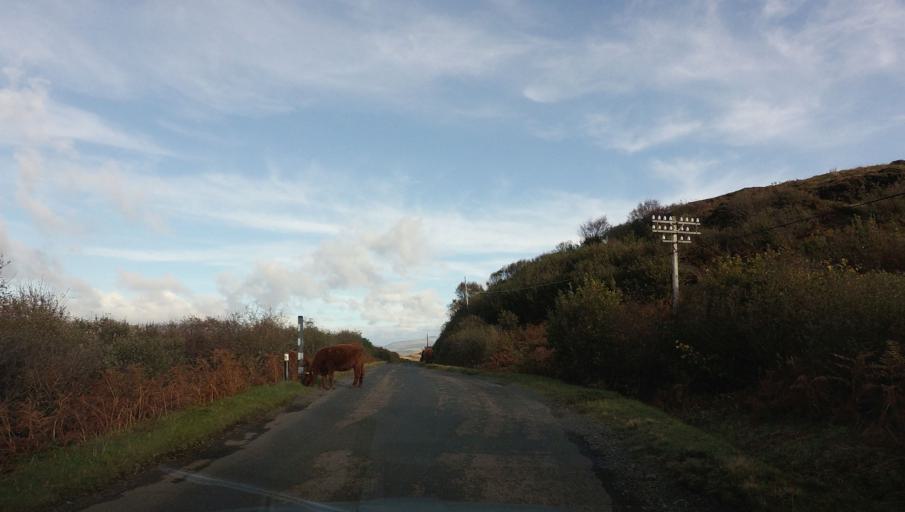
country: GB
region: Scotland
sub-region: Argyll and Bute
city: Isle Of Mull
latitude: 56.3302
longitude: -6.1950
